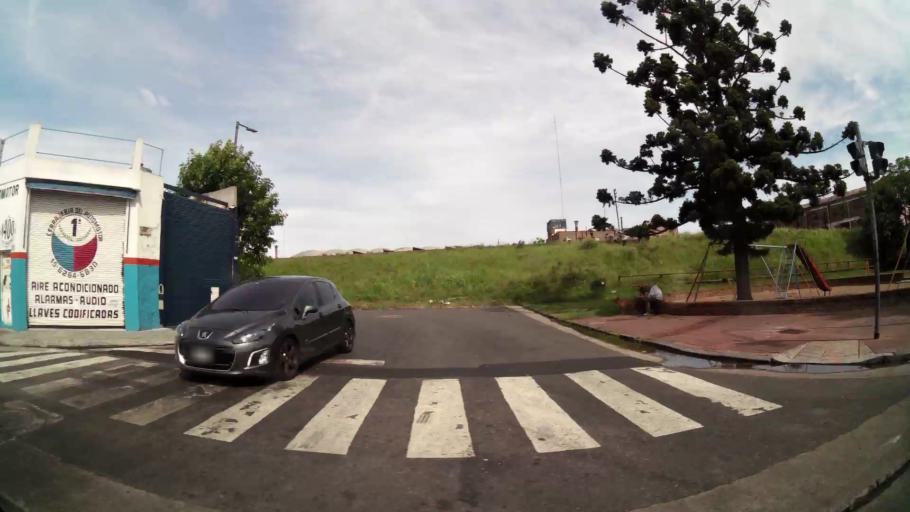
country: AR
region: Buenos Aires F.D.
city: Villa Lugano
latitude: -34.6473
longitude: -58.4274
